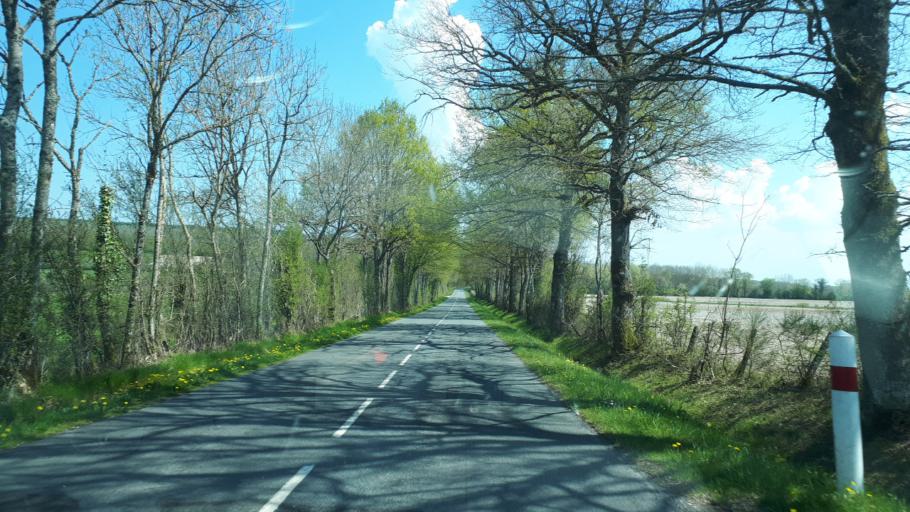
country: FR
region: Centre
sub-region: Departement du Cher
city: Henrichemont
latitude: 47.3053
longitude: 2.6335
